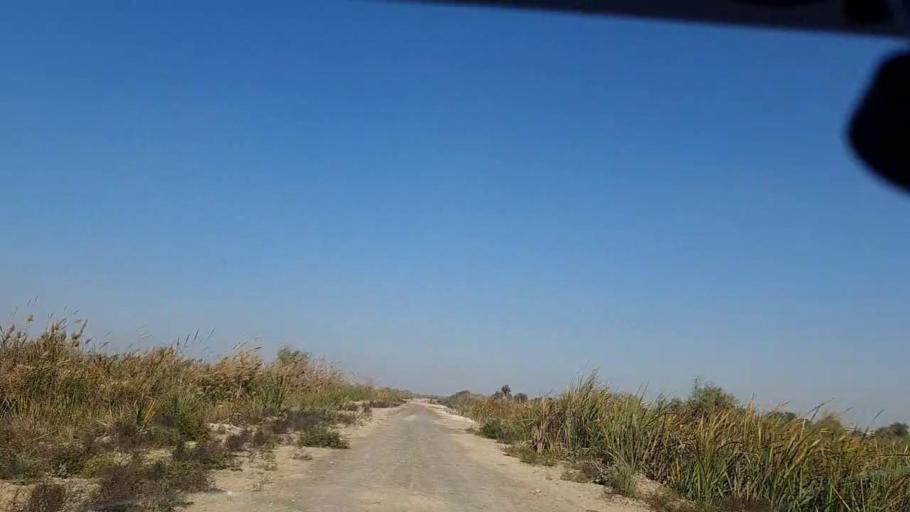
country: PK
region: Sindh
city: Khanpur
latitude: 27.5940
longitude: 69.3771
